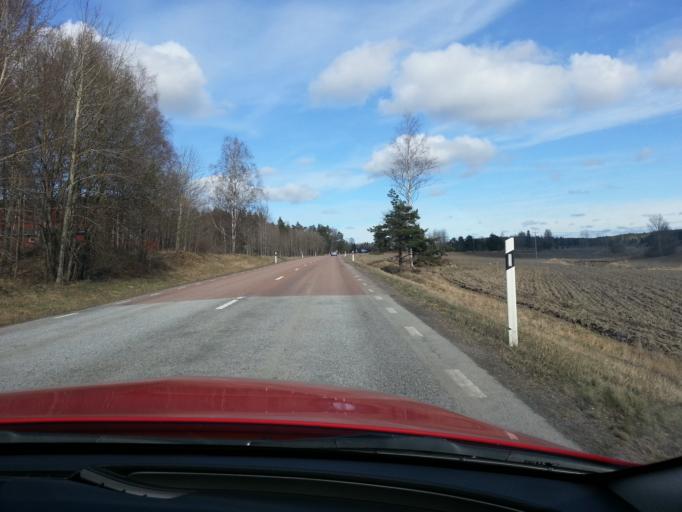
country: SE
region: Uppsala
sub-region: Osthammars Kommun
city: Gimo
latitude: 60.0665
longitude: 18.0872
